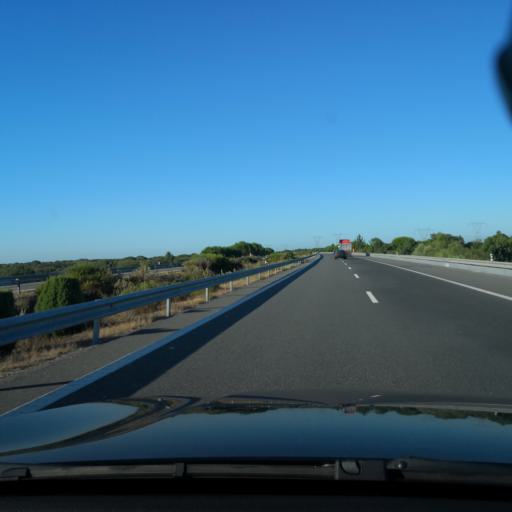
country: PT
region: Setubal
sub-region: Alcacer do Sal
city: Alcacer do Sal
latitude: 38.3382
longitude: -8.5035
